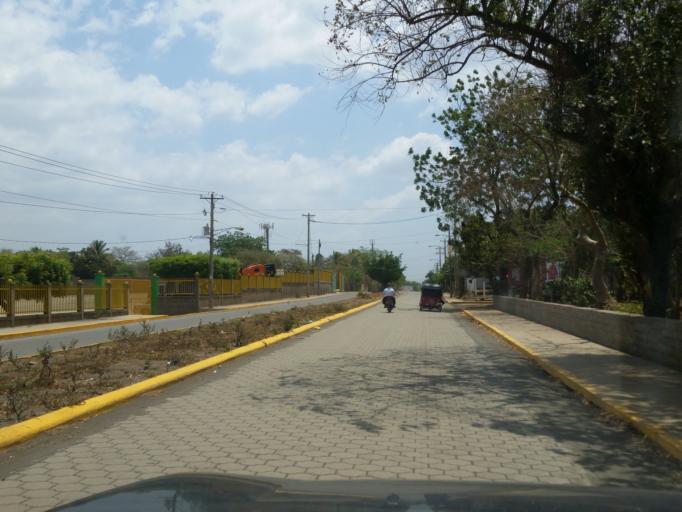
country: NI
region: Managua
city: Managua
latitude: 12.1356
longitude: -86.1847
